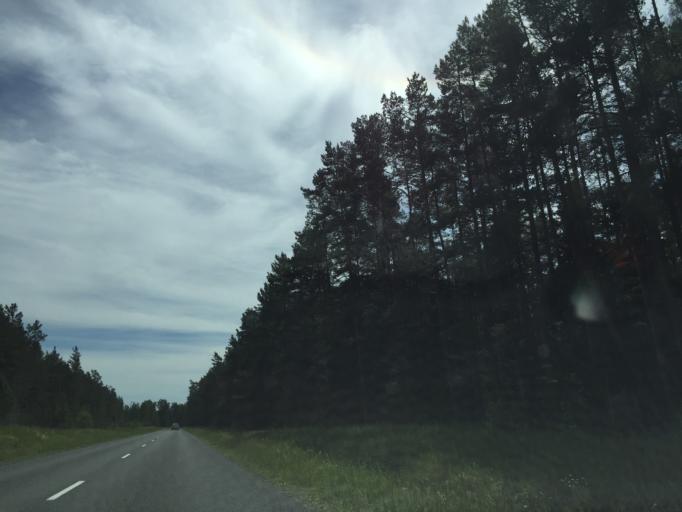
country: LV
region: Dundaga
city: Dundaga
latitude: 57.6636
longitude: 22.5701
